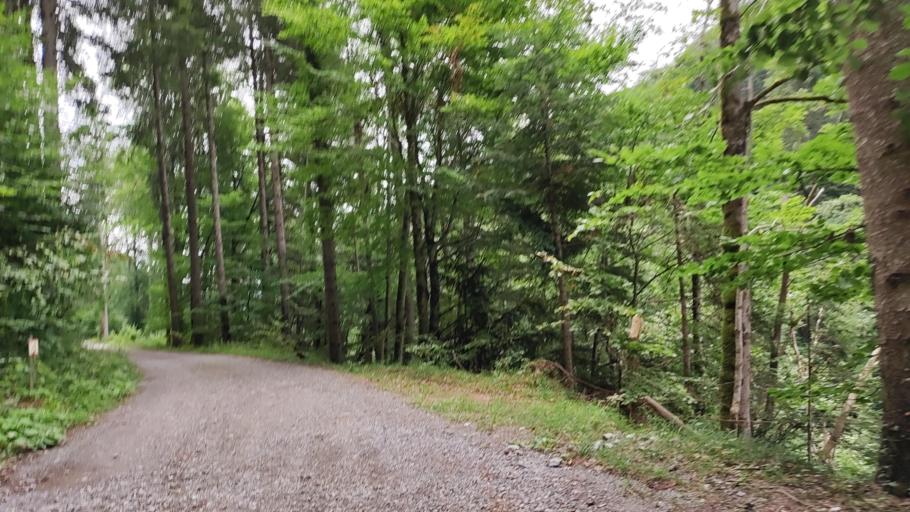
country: AT
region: Vorarlberg
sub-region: Politischer Bezirk Feldkirch
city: Feldkirch
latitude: 47.1978
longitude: 9.6051
